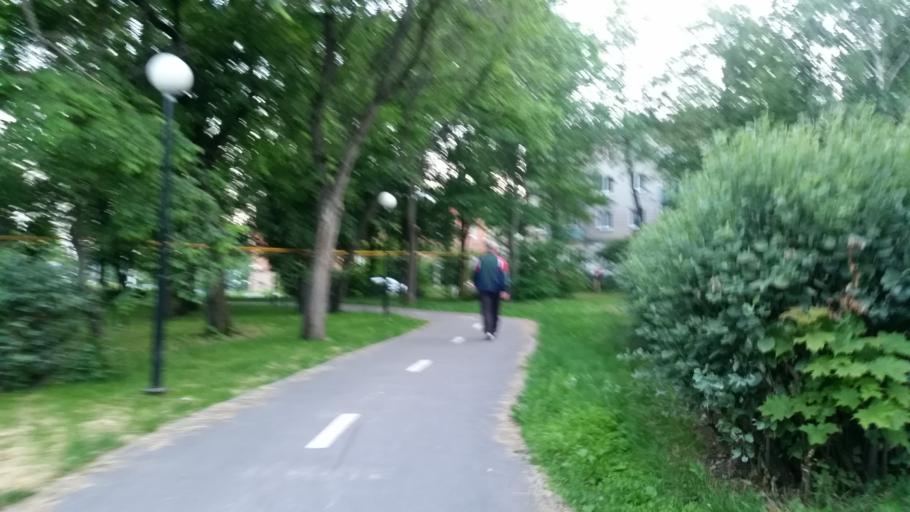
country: RU
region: Ulyanovsk
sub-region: Ulyanovskiy Rayon
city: Ulyanovsk
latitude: 54.3289
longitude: 48.4077
